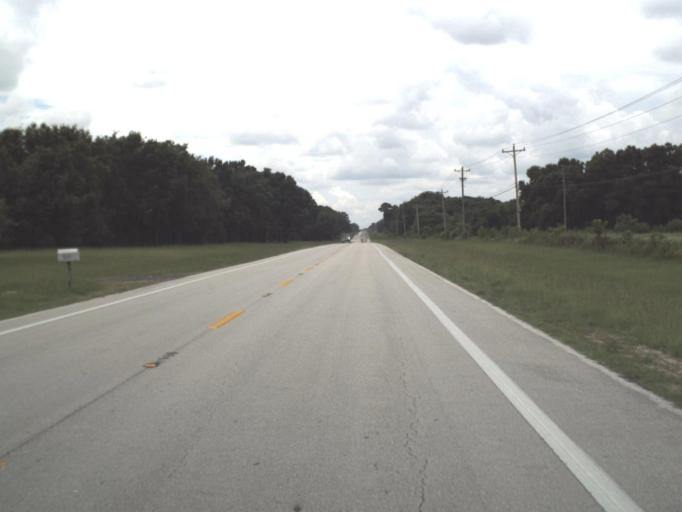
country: US
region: Florida
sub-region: Alachua County
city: Newberry
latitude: 29.6947
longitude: -82.6071
